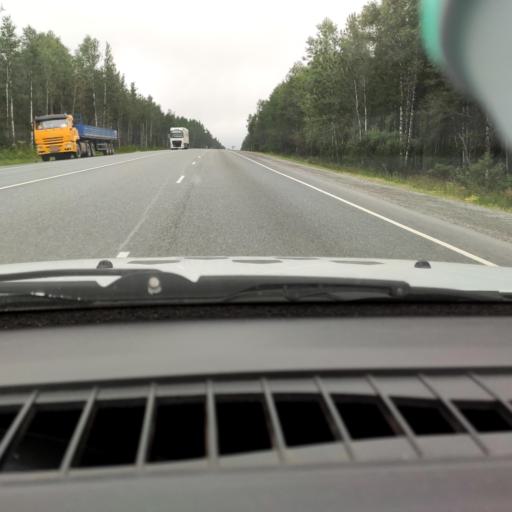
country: RU
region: Chelyabinsk
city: Zlatoust
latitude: 55.0407
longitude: 59.7246
